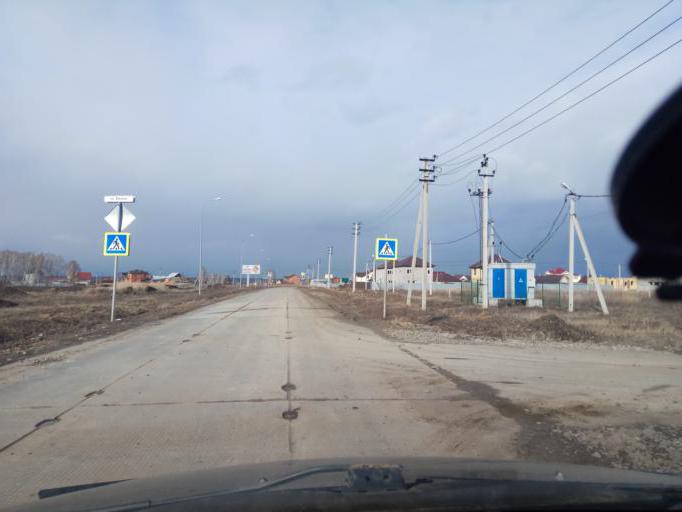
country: RU
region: Tjumen
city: Moskovskiy
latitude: 57.2161
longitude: 65.2586
